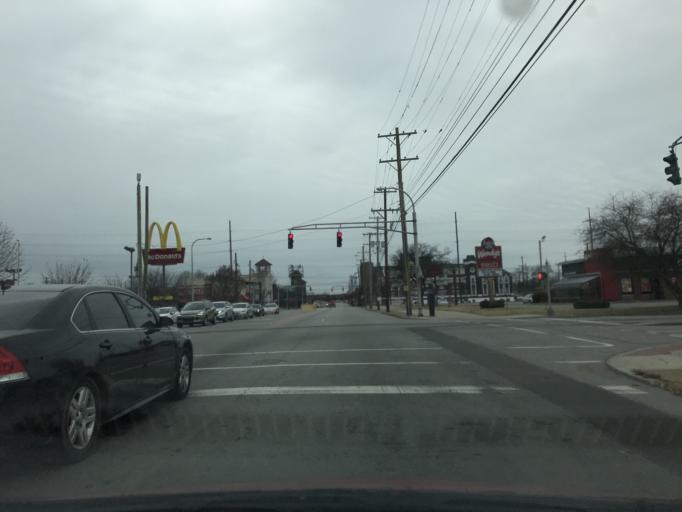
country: US
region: Kentucky
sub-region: Jefferson County
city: Louisville
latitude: 38.2476
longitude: -85.7709
